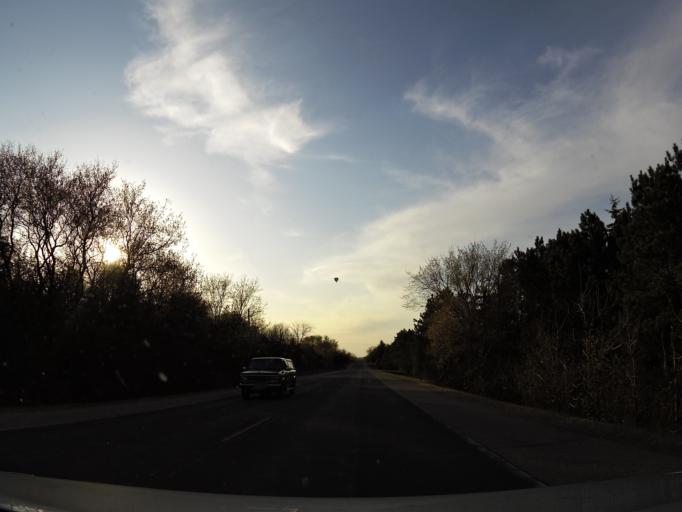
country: US
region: Minnesota
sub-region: Washington County
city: Lake Saint Croix Beach
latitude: 44.9350
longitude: -92.7171
